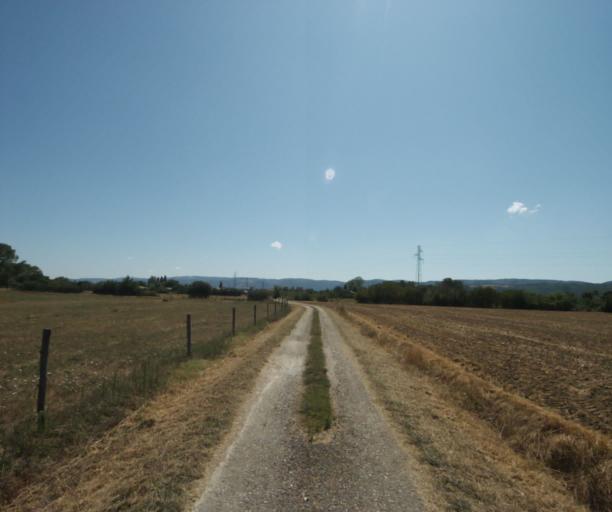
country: FR
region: Midi-Pyrenees
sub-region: Departement de la Haute-Garonne
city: Revel
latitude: 43.4691
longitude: 1.9868
